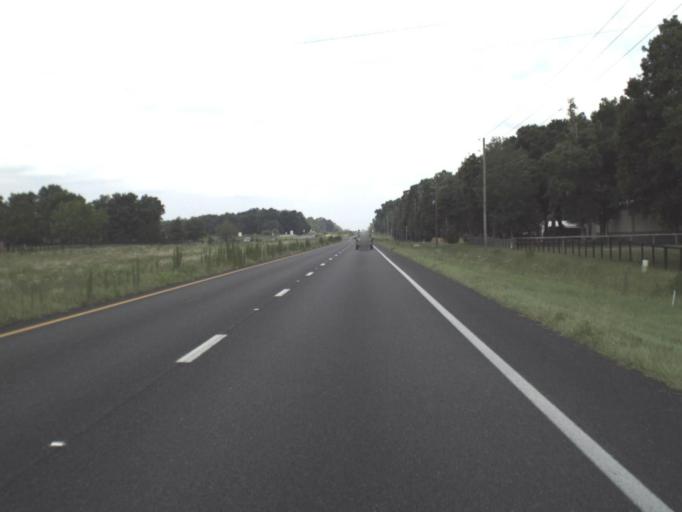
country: US
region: Florida
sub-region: Levy County
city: Williston Highlands
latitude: 29.4047
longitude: -82.5189
